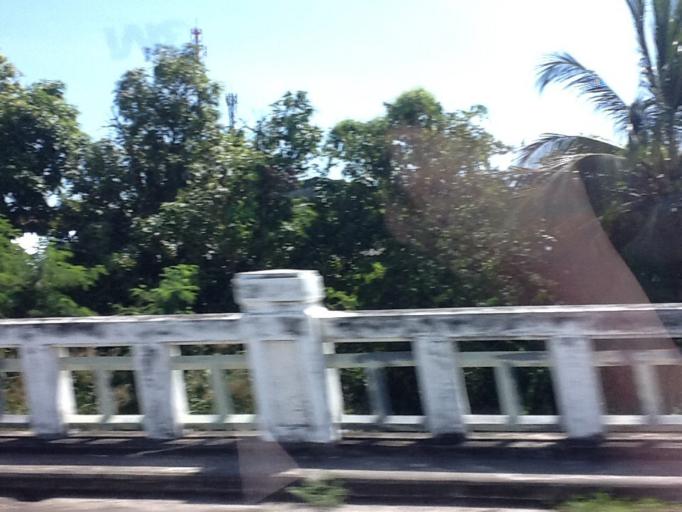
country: TH
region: Phuket
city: Ban Ko Kaeo
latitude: 7.9553
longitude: 98.3850
